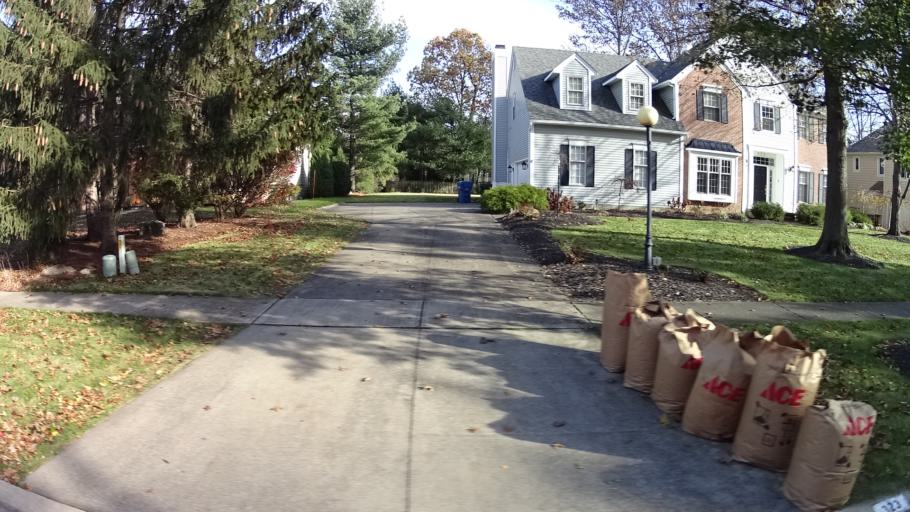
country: US
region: Ohio
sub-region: Cuyahoga County
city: Bay Village
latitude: 41.4995
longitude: -81.9733
